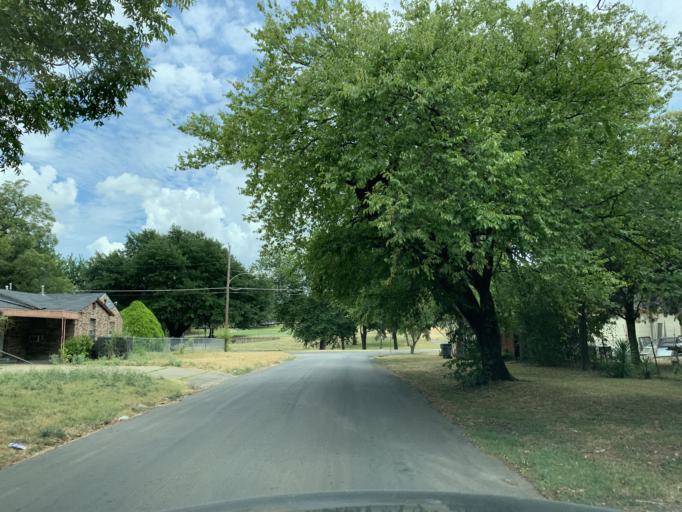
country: US
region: Texas
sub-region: Dallas County
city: Cockrell Hill
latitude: 32.7331
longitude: -96.8788
